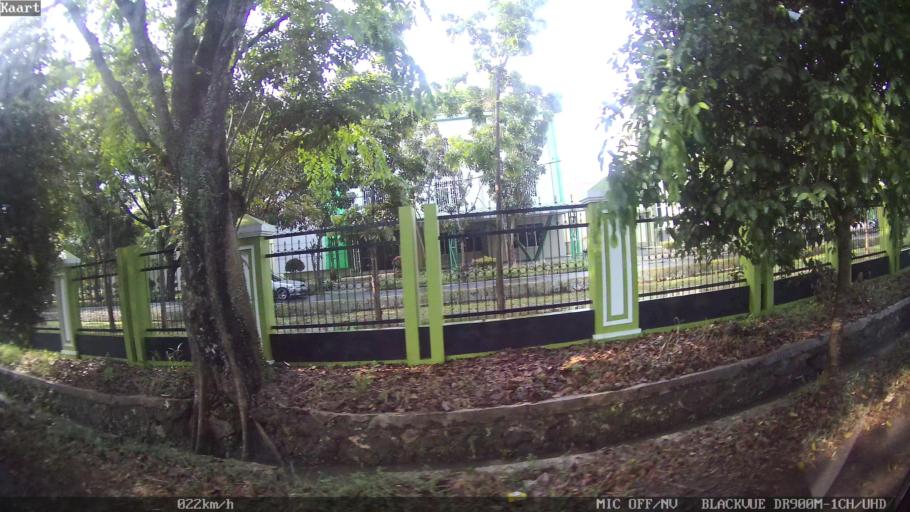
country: ID
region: Lampung
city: Kedaton
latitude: -5.3855
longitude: 105.3041
